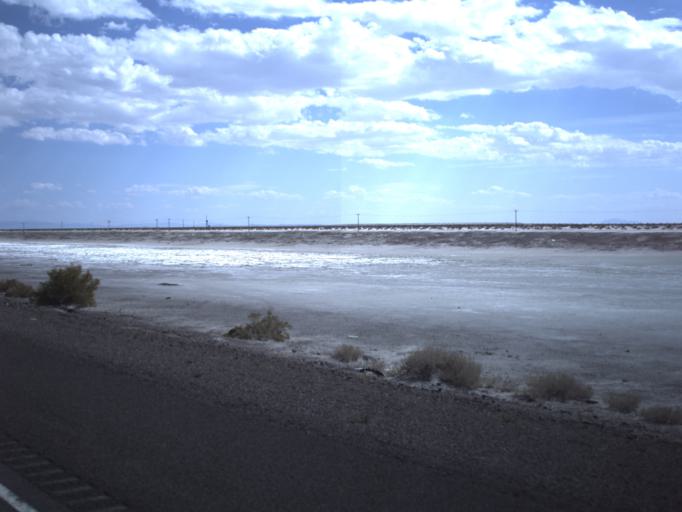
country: US
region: Utah
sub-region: Tooele County
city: Wendover
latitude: 40.7377
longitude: -113.8152
